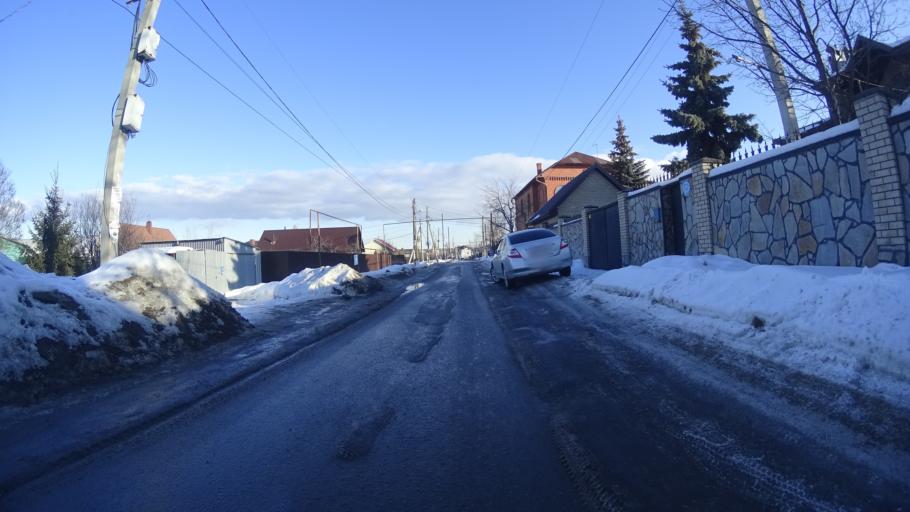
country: RU
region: Chelyabinsk
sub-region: Gorod Chelyabinsk
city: Chelyabinsk
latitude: 55.1551
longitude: 61.3075
